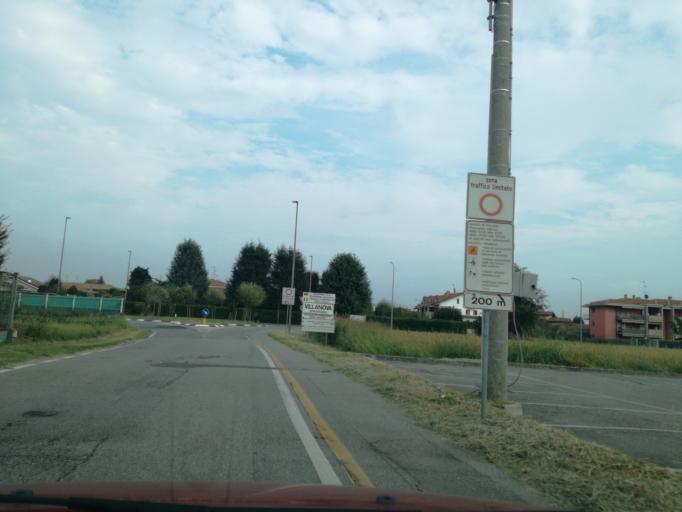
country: IT
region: Lombardy
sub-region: Provincia di Monza e Brianza
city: Villanova
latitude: 45.6411
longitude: 9.3874
